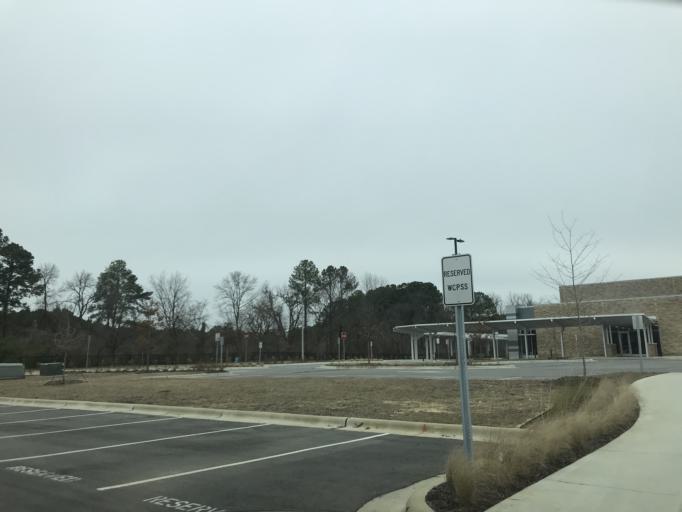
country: US
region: North Carolina
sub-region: Wake County
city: Raleigh
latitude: 35.7604
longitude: -78.6160
